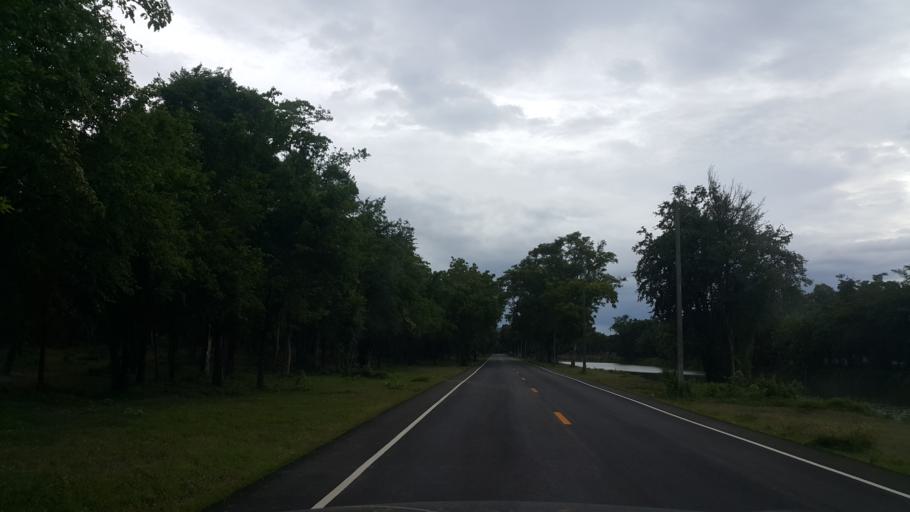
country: TH
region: Sukhothai
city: Ban Na
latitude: 17.0264
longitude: 99.7004
